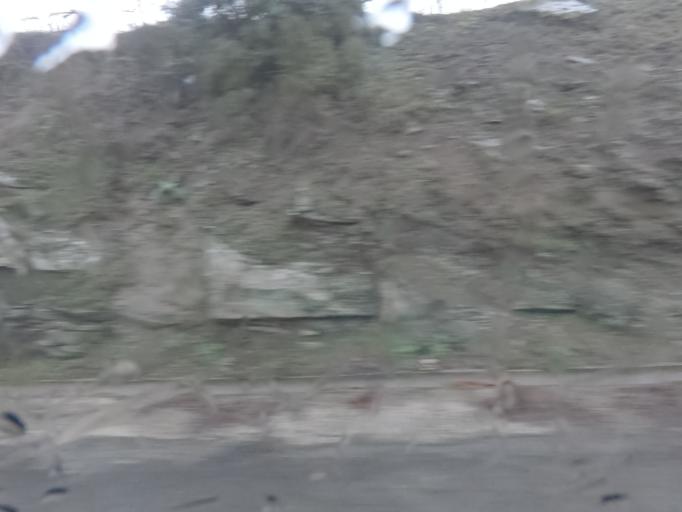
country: PT
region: Vila Real
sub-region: Peso da Regua
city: Peso da Regua
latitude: 41.1682
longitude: -7.7386
